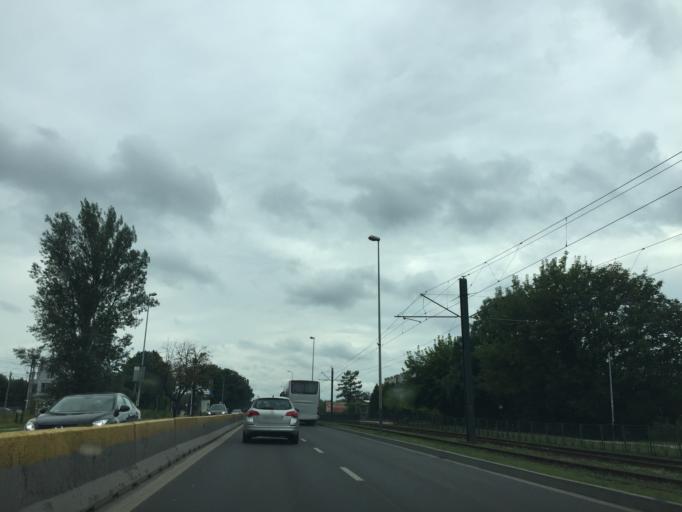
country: PL
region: Lesser Poland Voivodeship
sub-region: Krakow
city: Krakow
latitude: 50.0255
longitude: 19.9345
